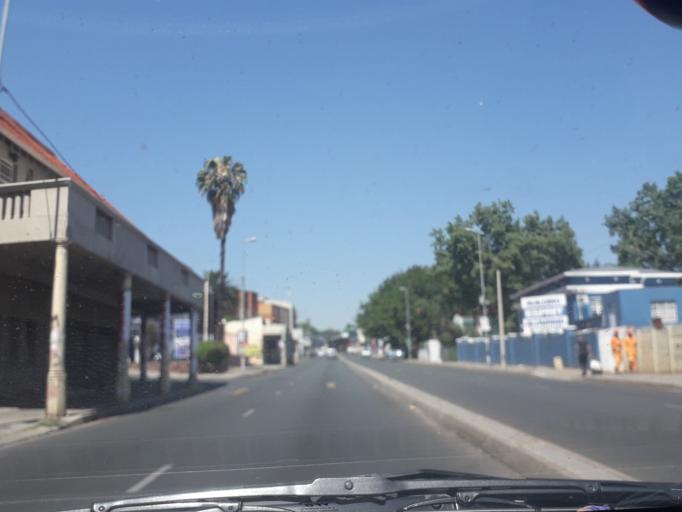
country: ZA
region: Gauteng
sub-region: City of Johannesburg Metropolitan Municipality
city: Johannesburg
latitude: -26.1666
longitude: 28.0794
